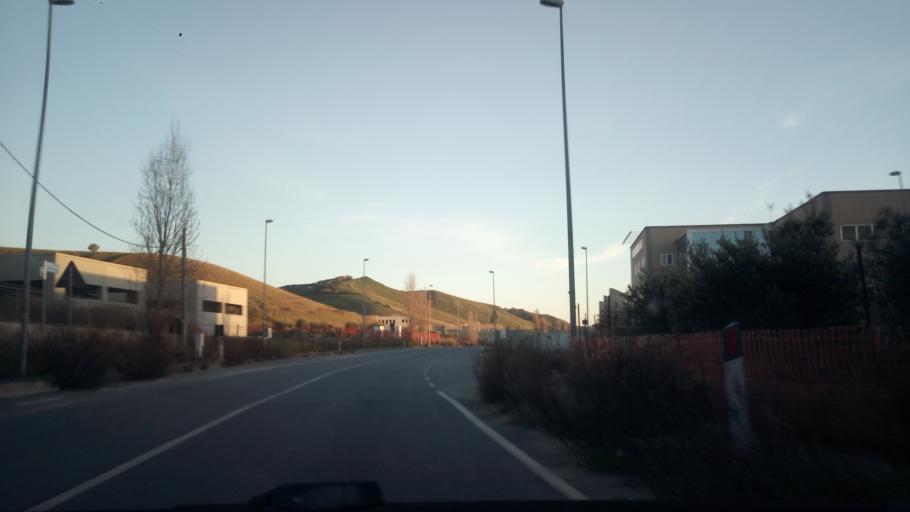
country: IT
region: Calabria
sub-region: Provincia di Catanzaro
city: Catanzaro
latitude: 38.8487
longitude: 16.5813
